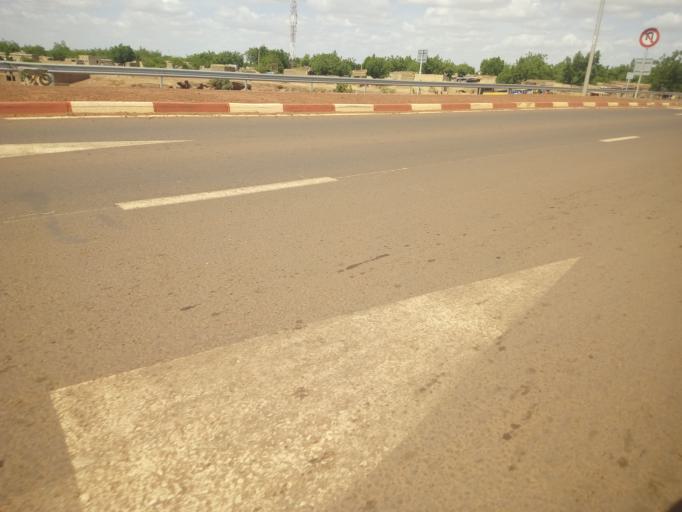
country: ML
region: Segou
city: Segou
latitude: 13.4266
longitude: -6.2199
